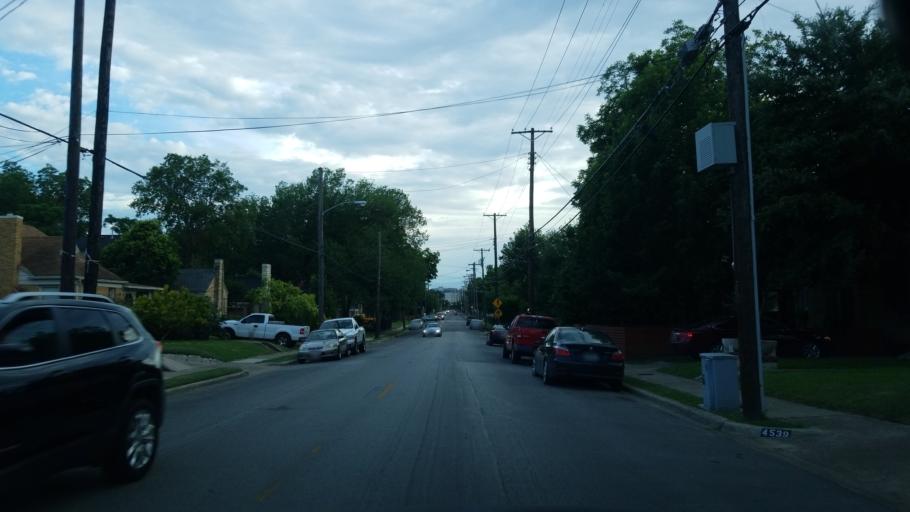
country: US
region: Texas
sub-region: Dallas County
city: Highland Park
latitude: 32.8089
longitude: -96.7851
